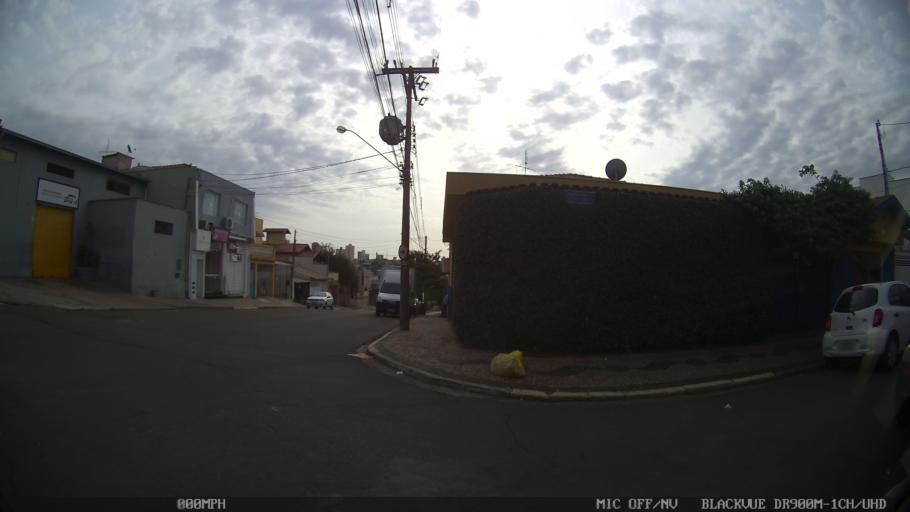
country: BR
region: Sao Paulo
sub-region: Piracicaba
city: Piracicaba
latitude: -22.7396
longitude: -47.6248
